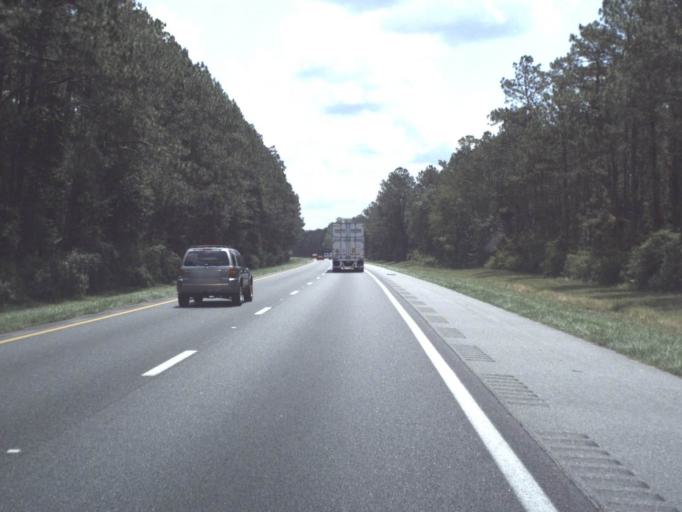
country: US
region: Florida
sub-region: Columbia County
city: Watertown
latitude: 30.2418
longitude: -82.5832
